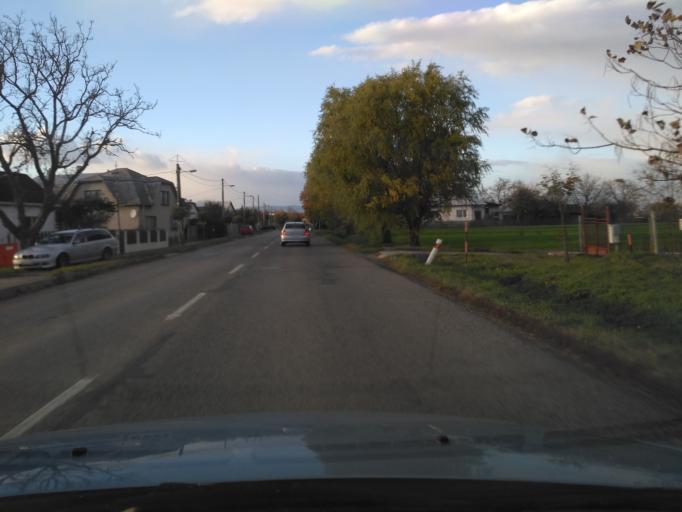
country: SK
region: Kosicky
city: Trebisov
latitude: 48.6419
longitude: 21.6830
